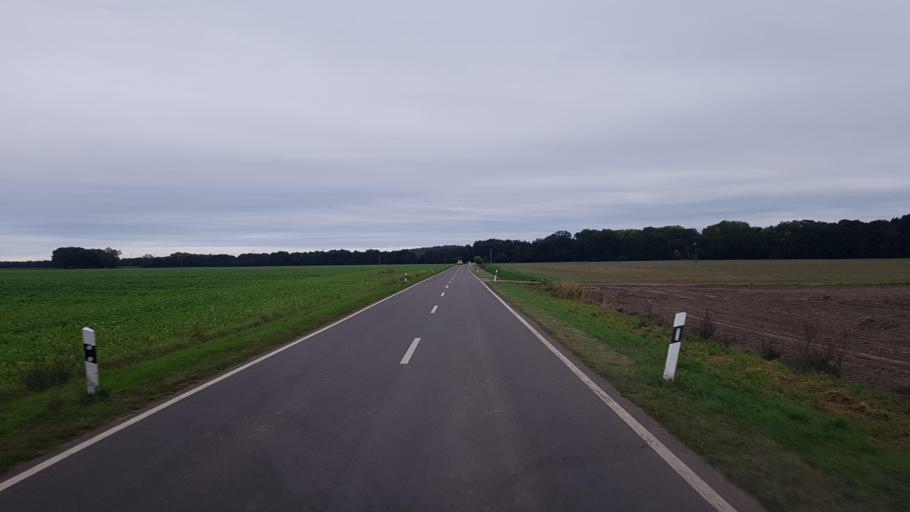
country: DE
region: Brandenburg
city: Drahnsdorf
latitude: 51.8957
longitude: 13.6318
